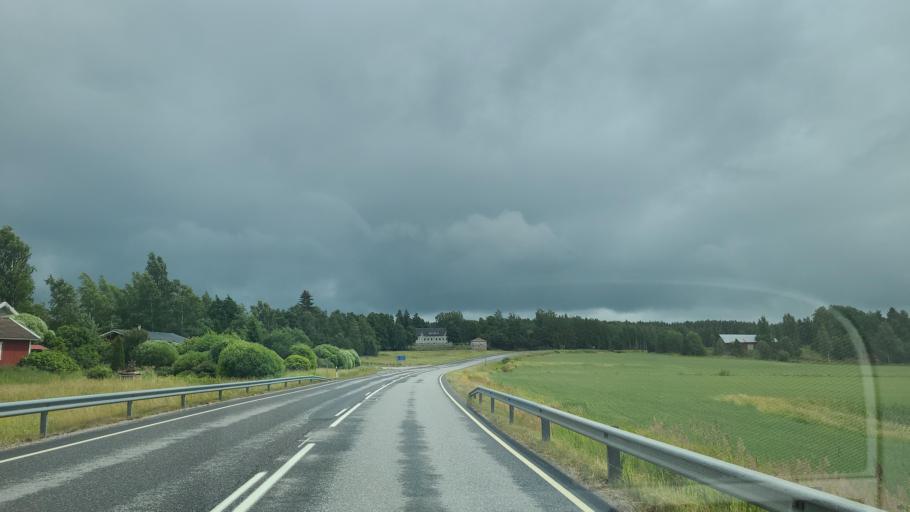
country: FI
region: Varsinais-Suomi
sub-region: Turku
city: Sauvo
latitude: 60.3318
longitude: 22.7112
